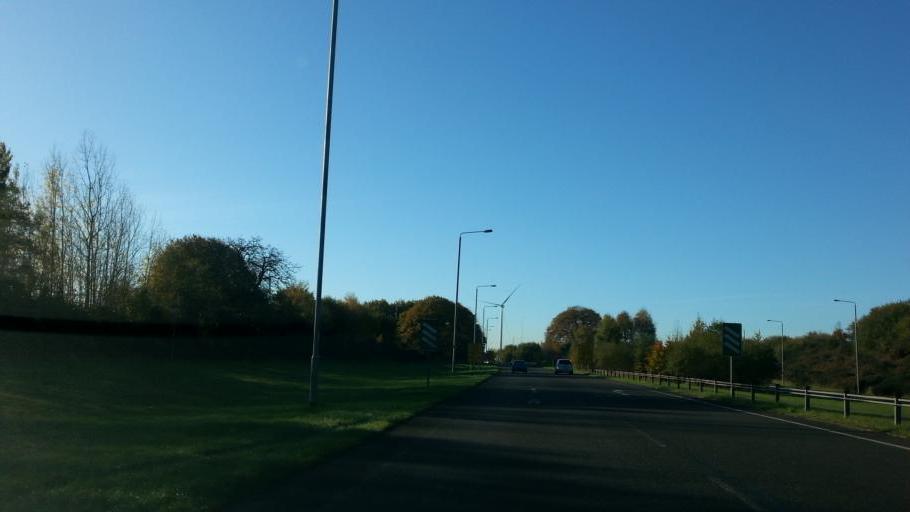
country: GB
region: England
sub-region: Nottinghamshire
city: Rainworth
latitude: 53.1279
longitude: -1.1391
